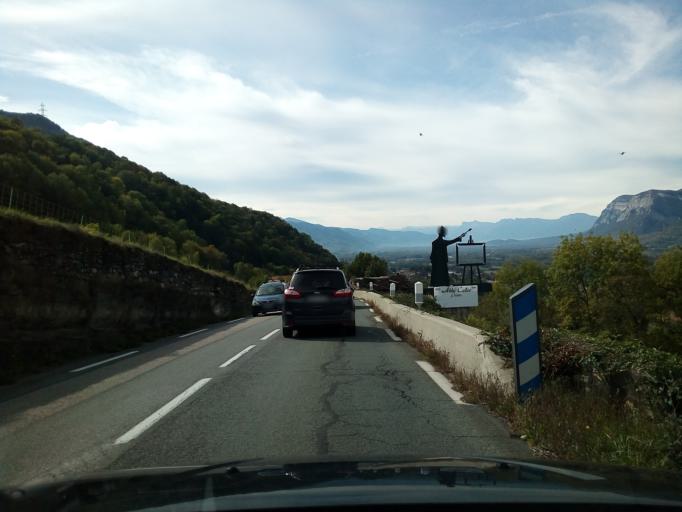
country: FR
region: Rhone-Alpes
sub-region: Departement de l'Isere
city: Le Cheylas
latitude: 45.3567
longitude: 5.9926
